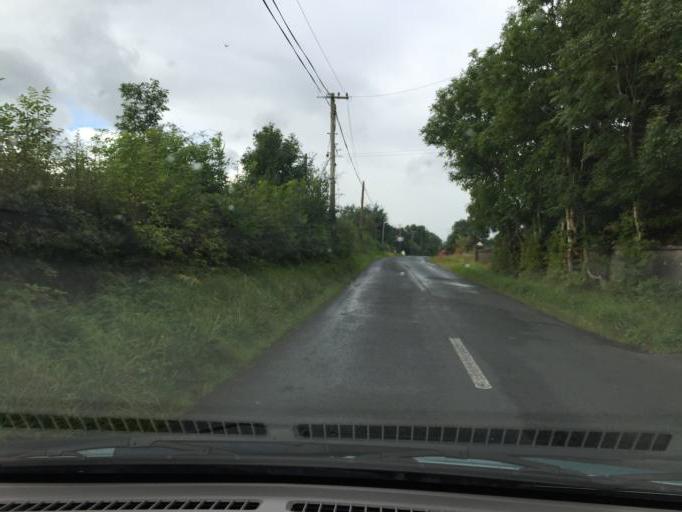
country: IE
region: Connaught
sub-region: Sligo
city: Tobercurry
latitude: 54.0381
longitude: -8.8248
